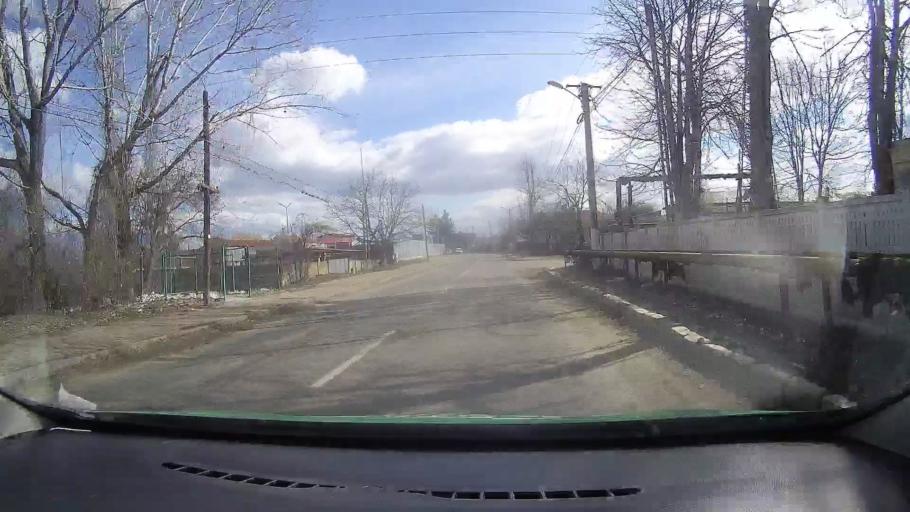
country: RO
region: Dambovita
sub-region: Municipiul Targoviste
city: Targoviste
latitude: 44.9416
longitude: 25.4400
